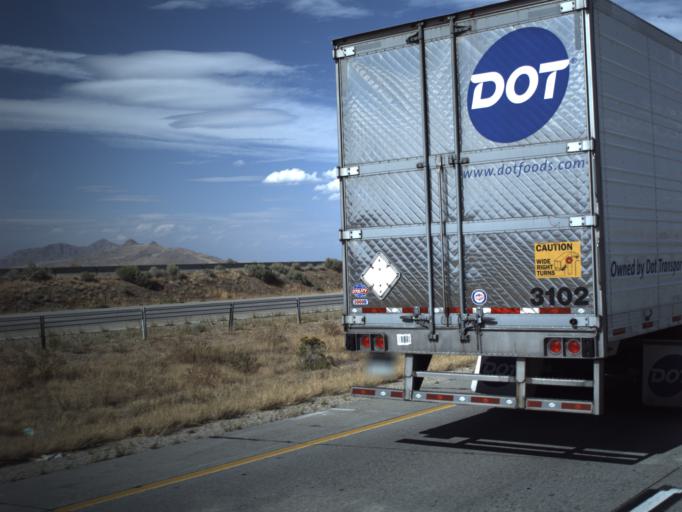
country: US
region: Utah
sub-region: Salt Lake County
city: Magna
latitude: 40.7557
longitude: -112.1703
